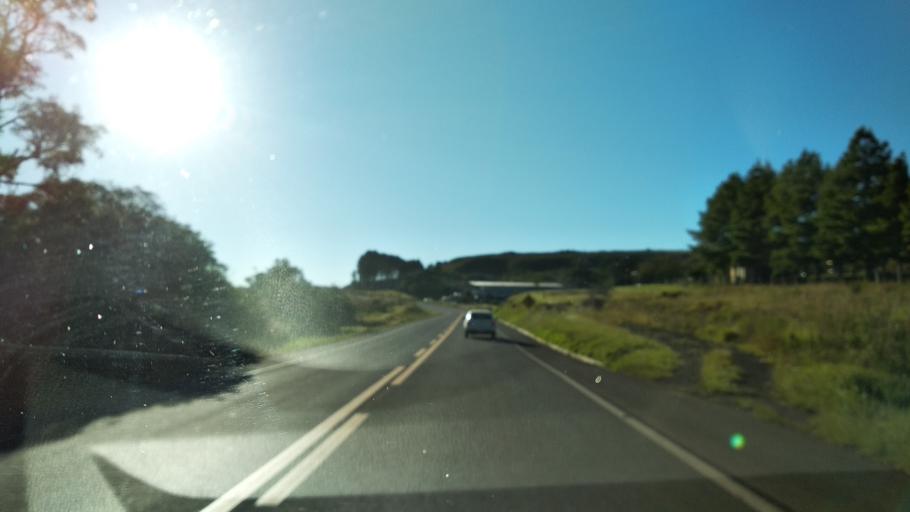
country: BR
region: Santa Catarina
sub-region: Lages
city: Lages
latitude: -27.7882
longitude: -50.4312
